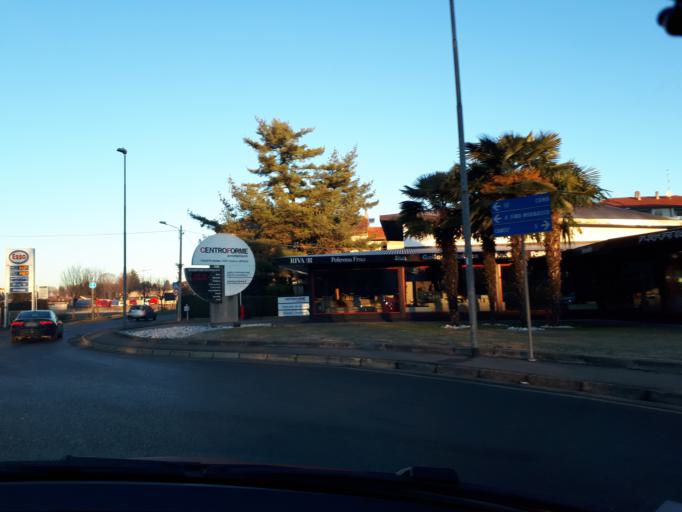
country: IT
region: Lombardy
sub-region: Provincia di Como
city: Cermenate
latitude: 45.7044
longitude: 9.0913
